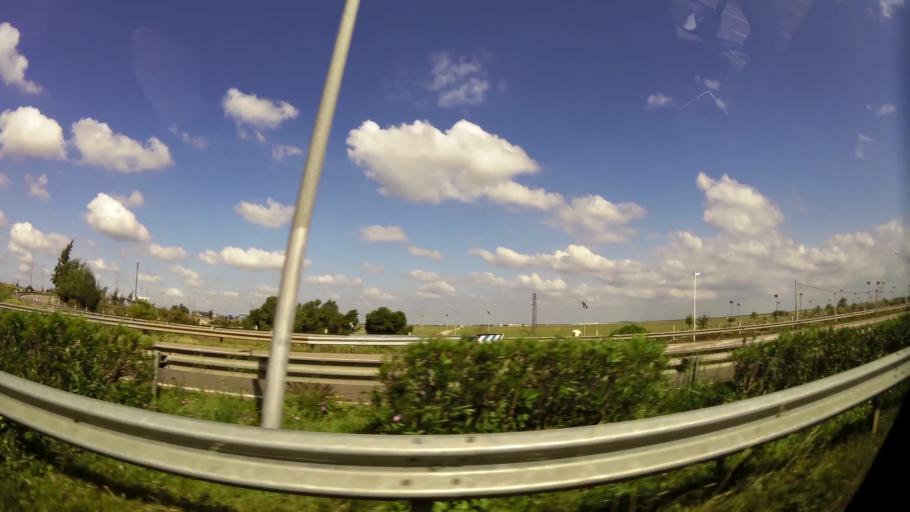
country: MA
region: Chaouia-Ouardigha
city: Nouaseur
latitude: 33.3883
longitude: -7.6199
